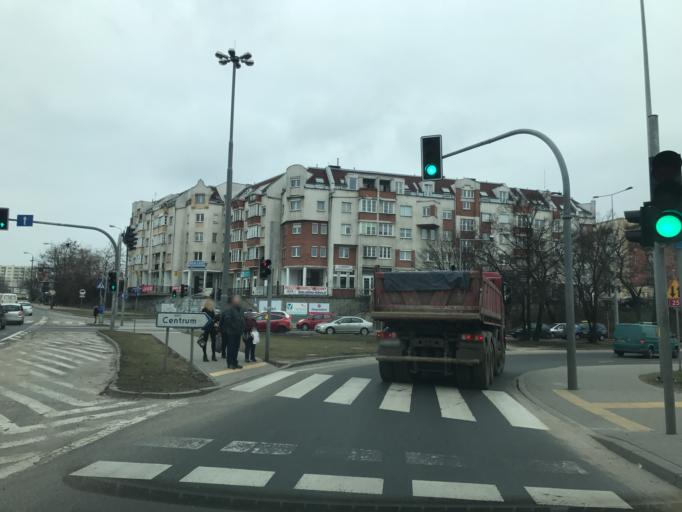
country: PL
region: Kujawsko-Pomorskie
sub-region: Bydgoszcz
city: Bydgoszcz
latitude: 53.1150
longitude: 18.0077
